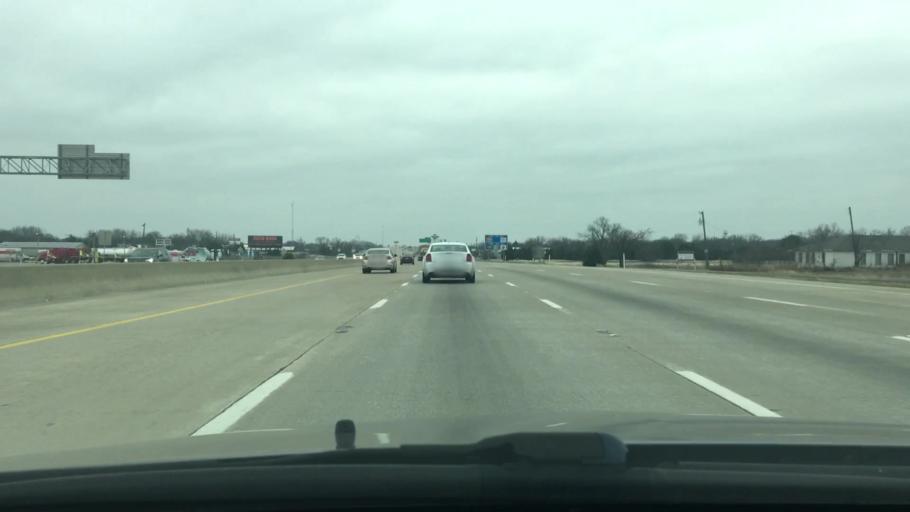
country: US
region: Texas
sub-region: Dallas County
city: Wilmer
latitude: 32.6043
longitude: -96.6862
